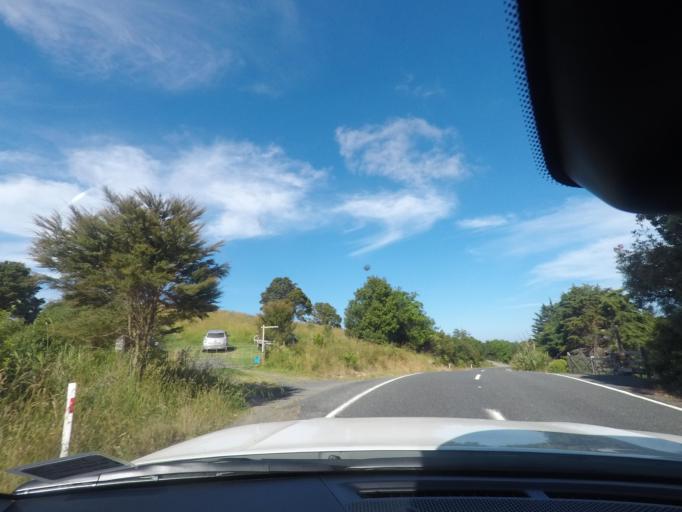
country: NZ
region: Northland
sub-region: Whangarei
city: Ngunguru
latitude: -35.6713
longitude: 174.4680
